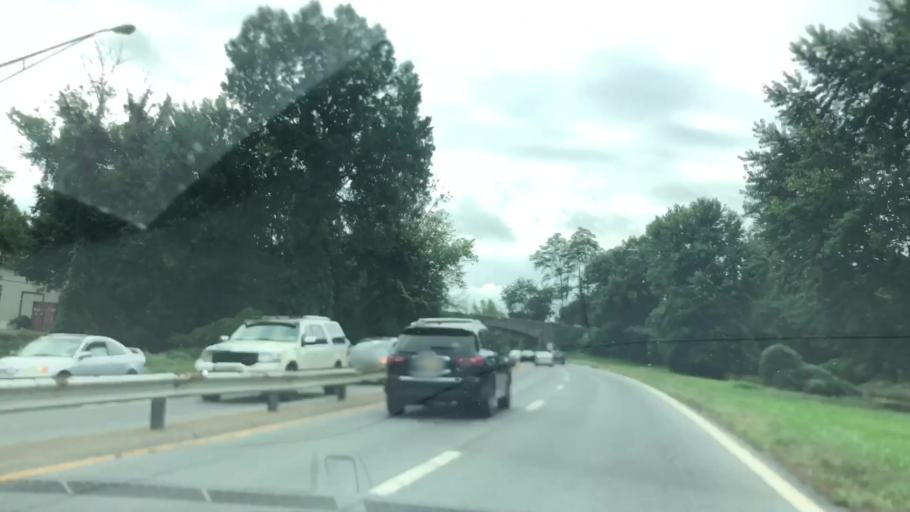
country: US
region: New York
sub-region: Westchester County
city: Hastings-on-Hudson
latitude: 40.9680
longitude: -73.8712
